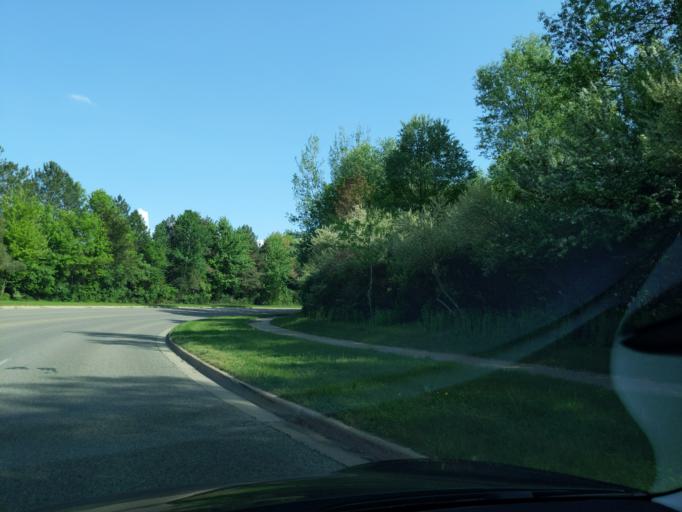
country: US
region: Michigan
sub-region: Ingham County
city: Okemos
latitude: 42.7209
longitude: -84.4098
